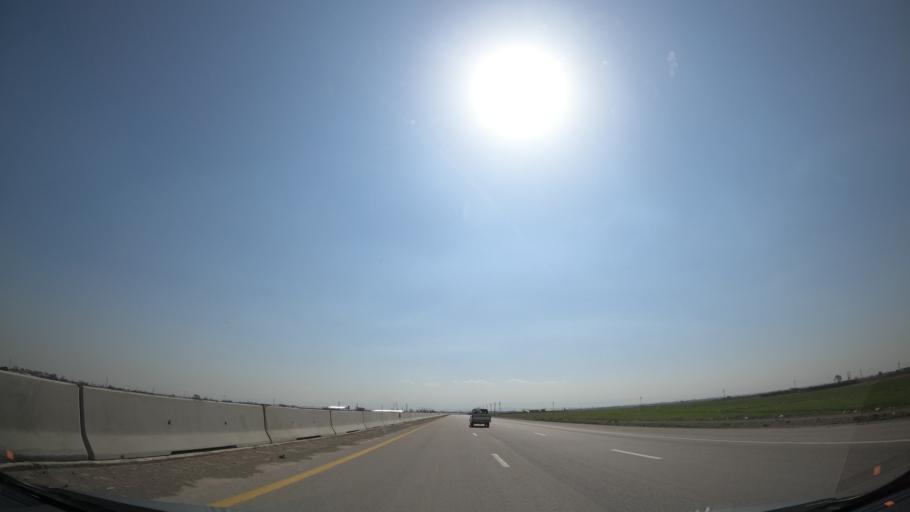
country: IR
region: Qazvin
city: Abyek
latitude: 35.9988
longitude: 50.4617
